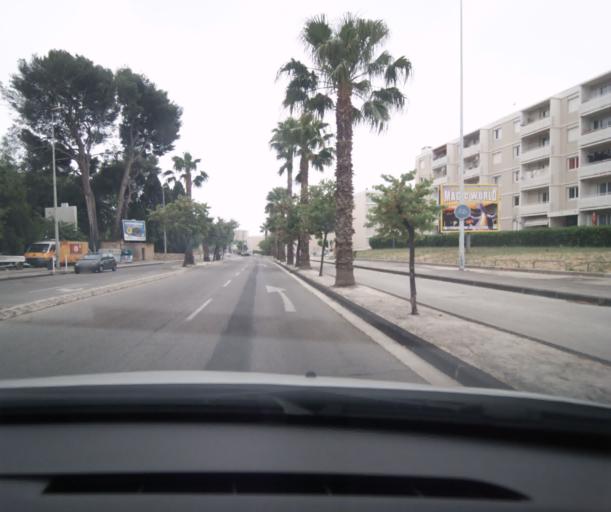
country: FR
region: Provence-Alpes-Cote d'Azur
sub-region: Departement du Var
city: La Valette-du-Var
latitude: 43.1274
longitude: 5.9815
